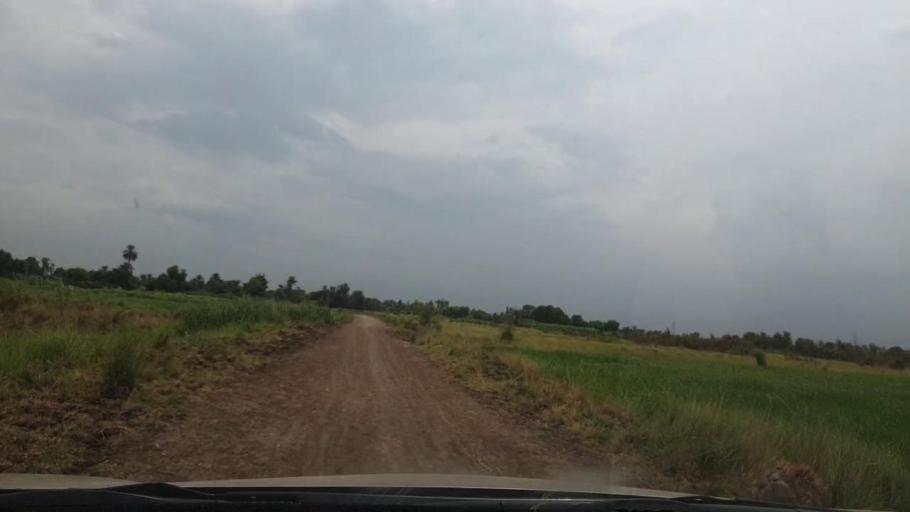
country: PK
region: Sindh
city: Ratodero
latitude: 27.7983
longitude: 68.3130
